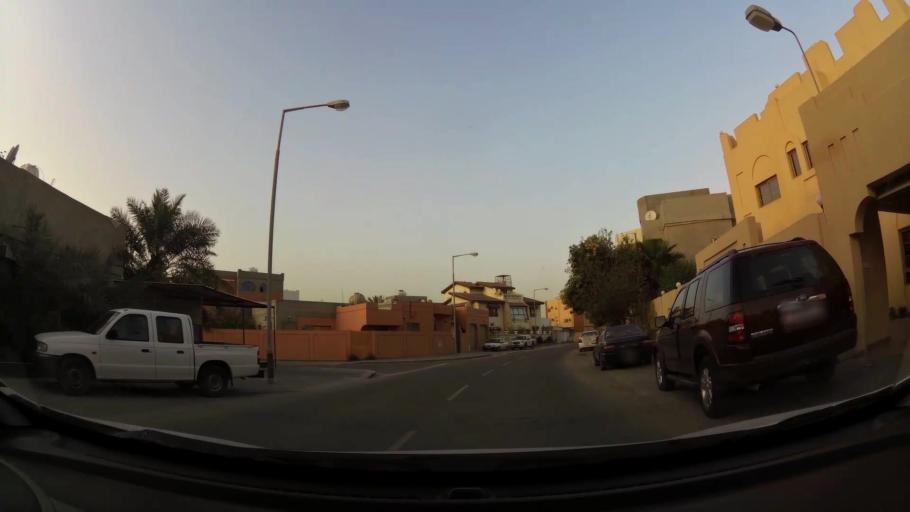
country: BH
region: Northern
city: Madinat `Isa
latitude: 26.1909
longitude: 50.4841
